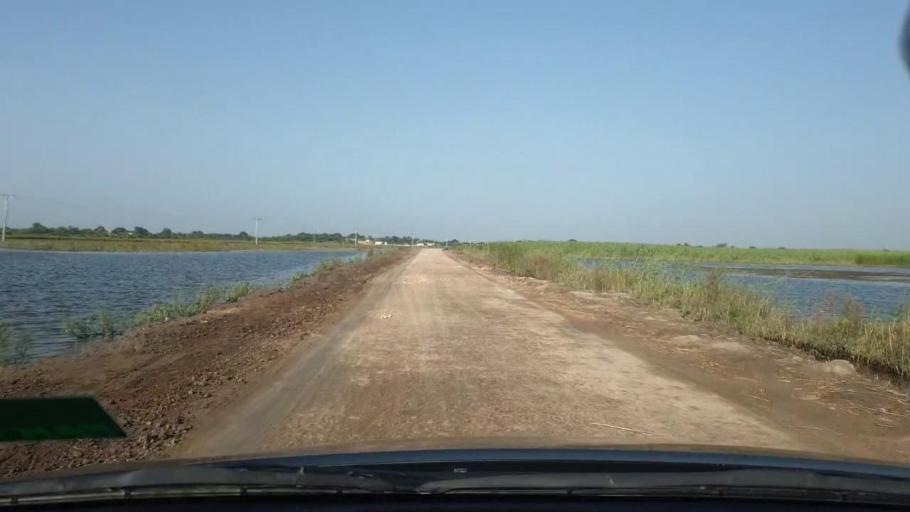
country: PK
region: Sindh
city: Tando Bago
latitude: 24.7231
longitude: 68.9507
